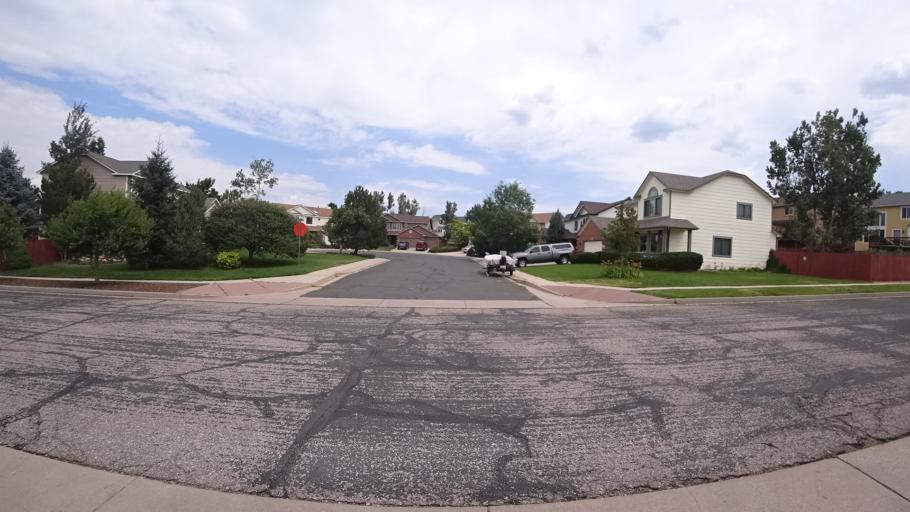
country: US
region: Colorado
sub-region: El Paso County
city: Black Forest
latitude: 38.9598
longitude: -104.7723
